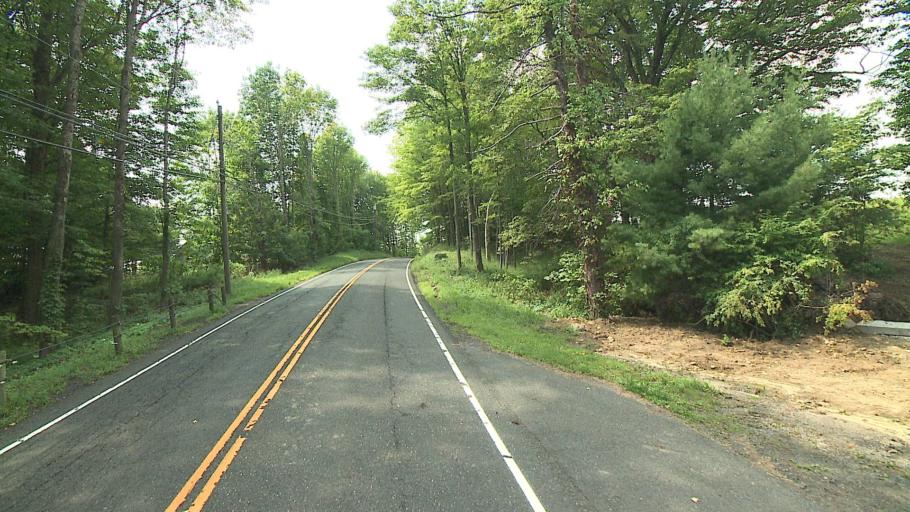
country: US
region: Connecticut
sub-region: Litchfield County
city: New Preston
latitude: 41.6346
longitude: -73.3506
